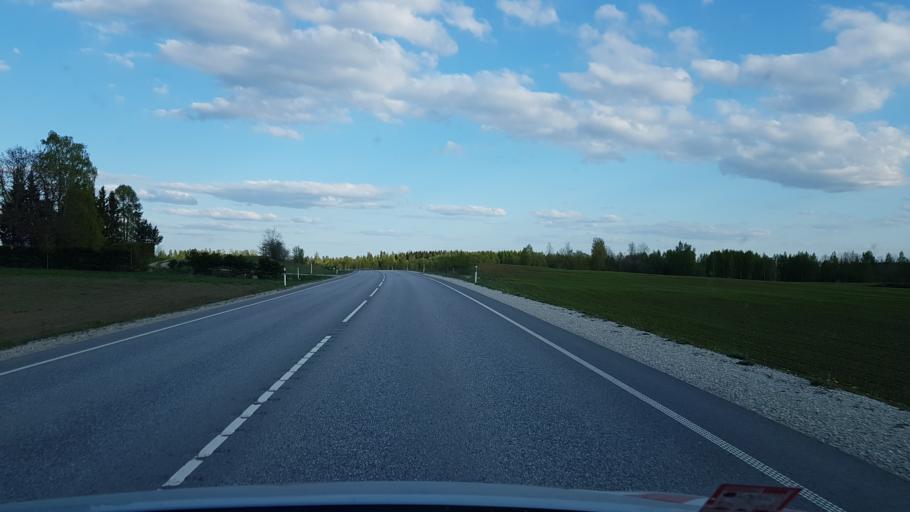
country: EE
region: Vorumaa
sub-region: Voru linn
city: Voru
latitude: 57.9250
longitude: 26.8024
